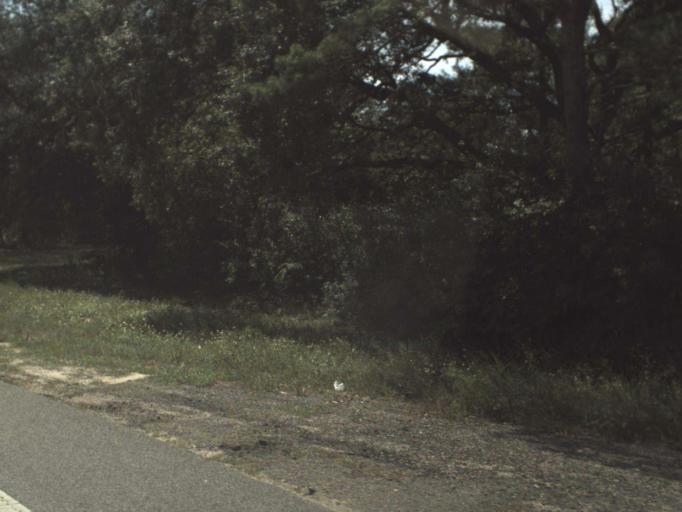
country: US
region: Florida
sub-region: Bay County
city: Lynn Haven
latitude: 30.5019
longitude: -85.6606
